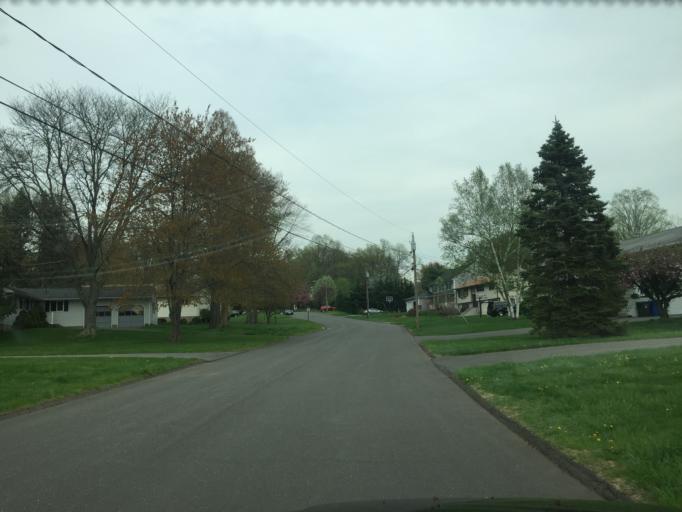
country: US
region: Connecticut
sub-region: Hartford County
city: Newington
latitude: 41.6816
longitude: -72.7452
